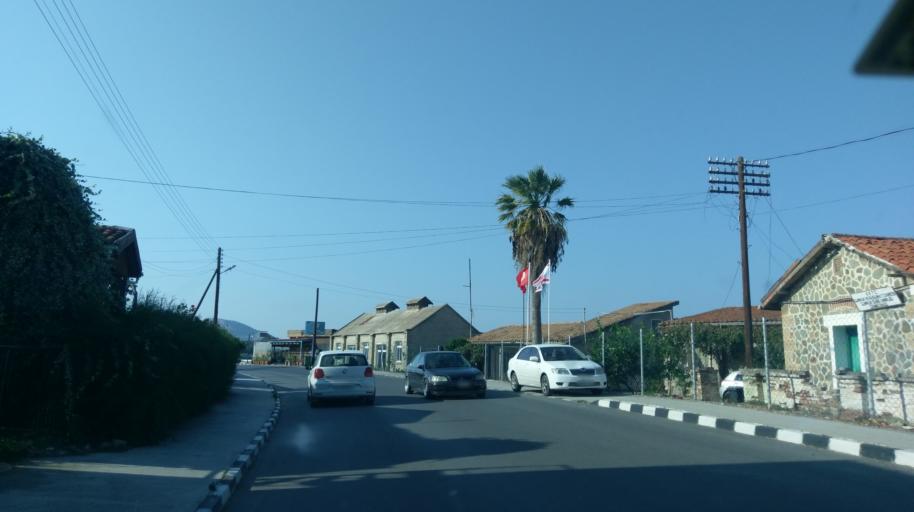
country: CY
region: Lefkosia
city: Lefka
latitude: 35.1416
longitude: 32.8227
